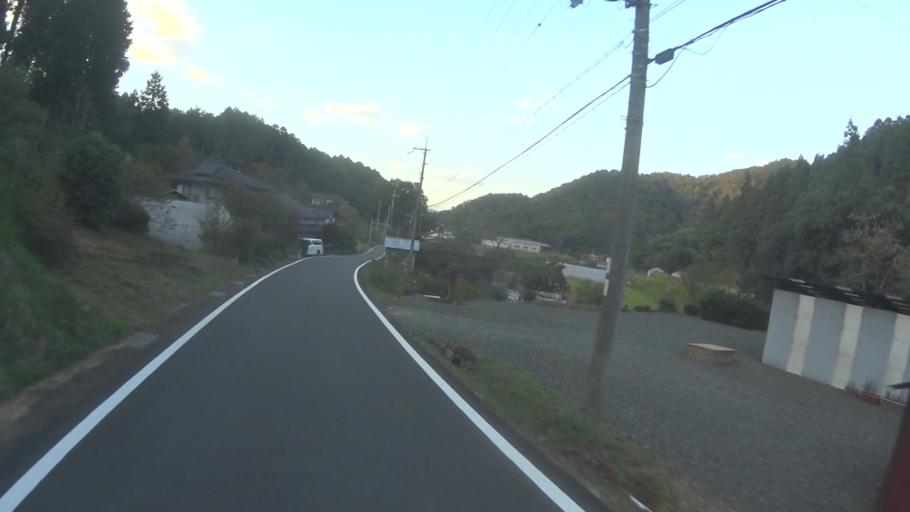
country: JP
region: Kyoto
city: Ayabe
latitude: 35.2864
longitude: 135.2381
